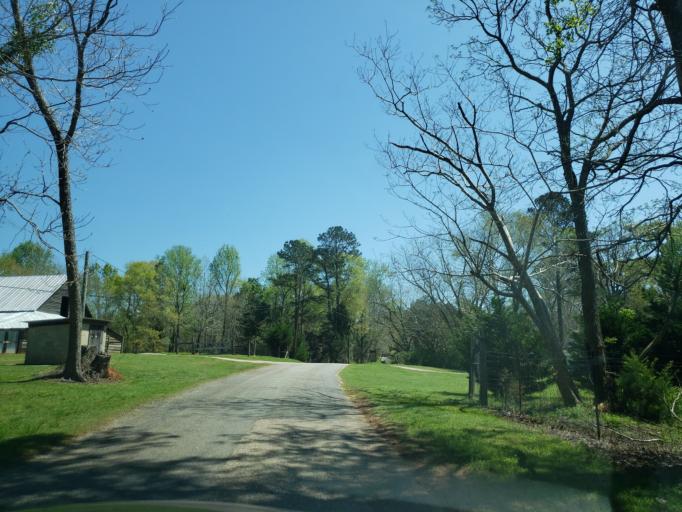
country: US
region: Alabama
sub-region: Elmore County
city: Tallassee
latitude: 32.6664
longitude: -85.8512
